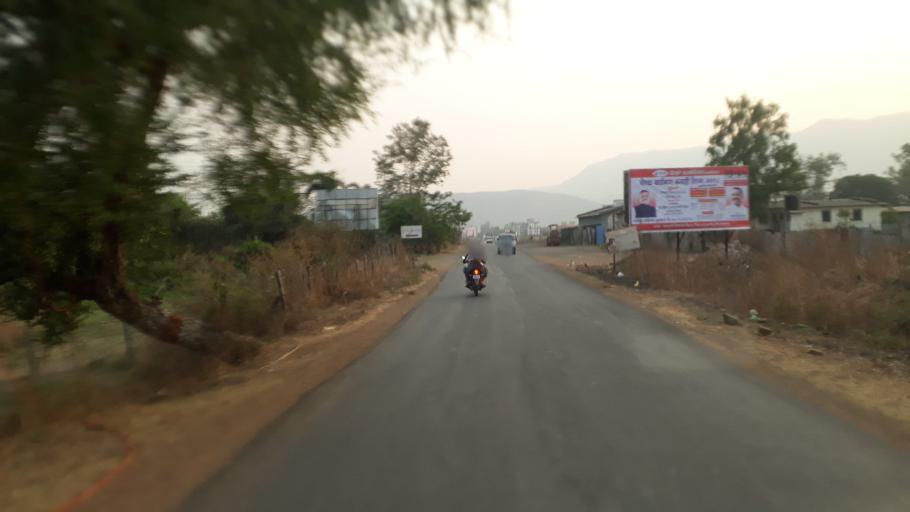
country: IN
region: Maharashtra
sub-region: Raigarh
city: Neral
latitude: 19.0370
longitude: 73.3281
